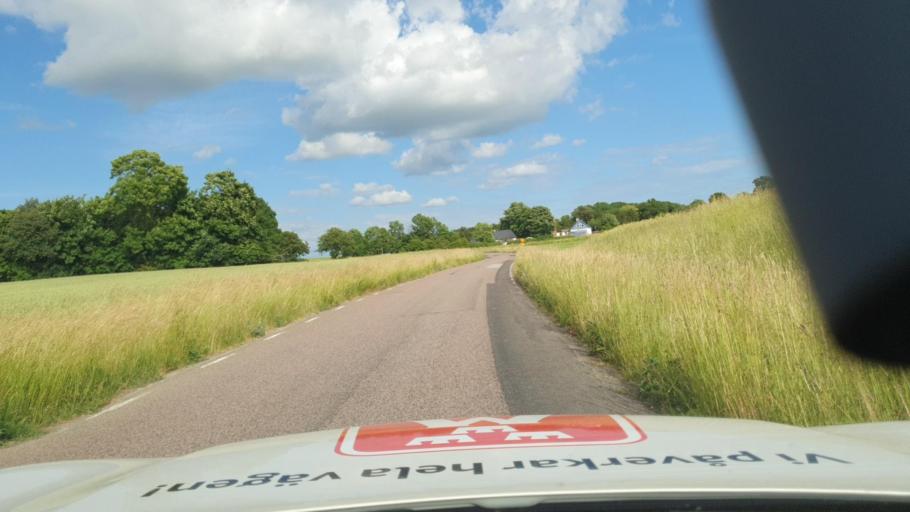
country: SE
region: Skane
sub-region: Skurups Kommun
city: Skivarp
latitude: 55.4530
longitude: 13.5408
